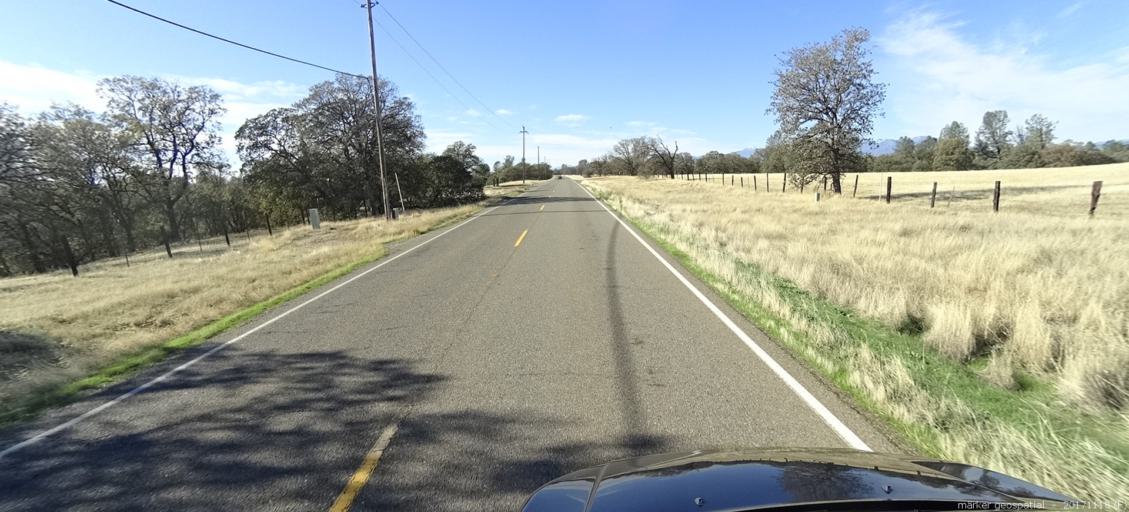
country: US
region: California
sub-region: Shasta County
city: Anderson
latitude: 40.4412
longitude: -122.3508
